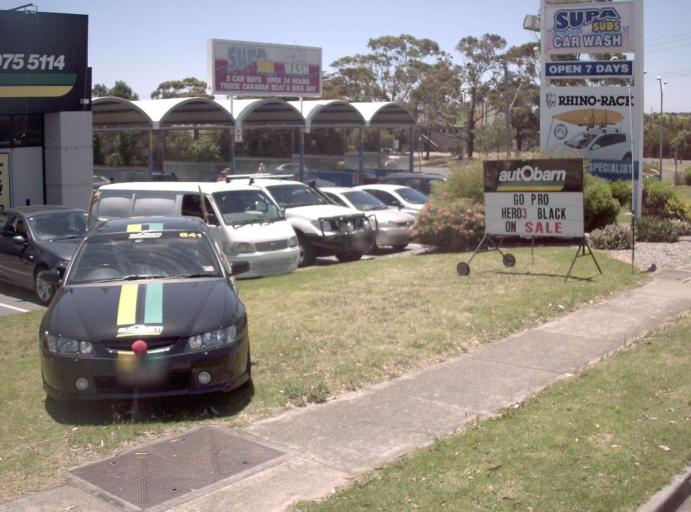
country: AU
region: Victoria
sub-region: Mornington Peninsula
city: Mornington
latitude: -38.2333
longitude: 145.0398
